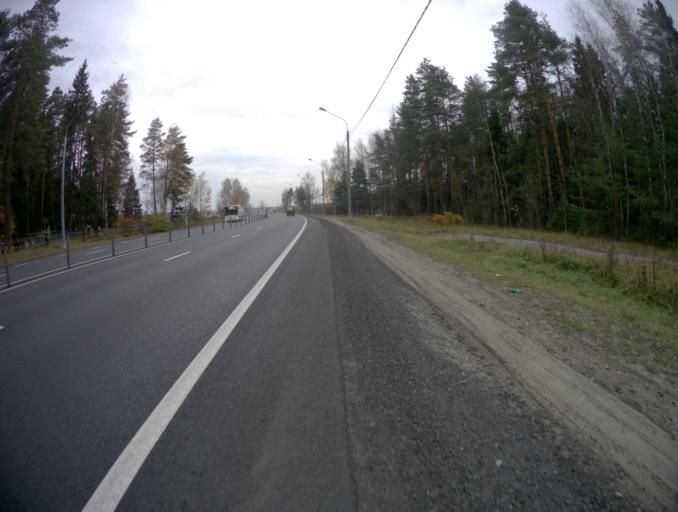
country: RU
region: Moskovskaya
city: Malaya Dubna
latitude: 55.8686
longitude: 38.9642
